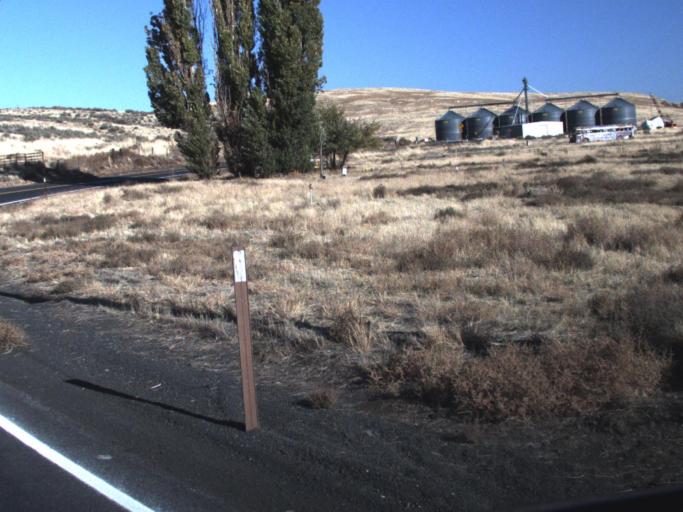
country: US
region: Washington
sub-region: Adams County
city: Ritzville
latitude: 46.7590
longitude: -118.3077
